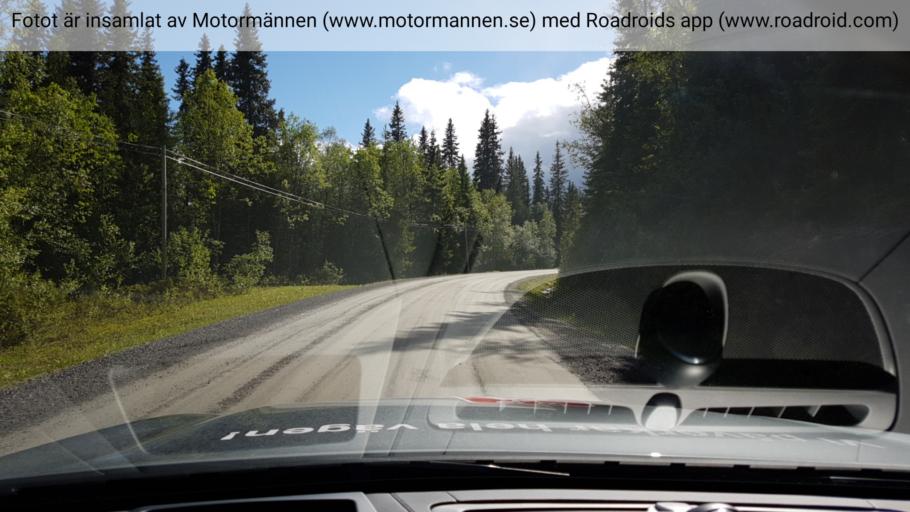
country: SE
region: Jaemtland
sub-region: Are Kommun
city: Are
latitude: 63.6941
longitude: 12.9332
